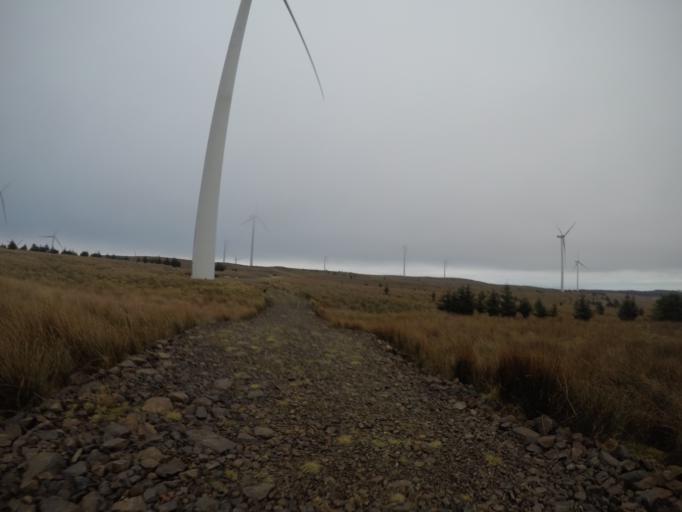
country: GB
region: Scotland
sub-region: North Ayrshire
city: Fairlie
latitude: 55.7364
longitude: -4.7897
